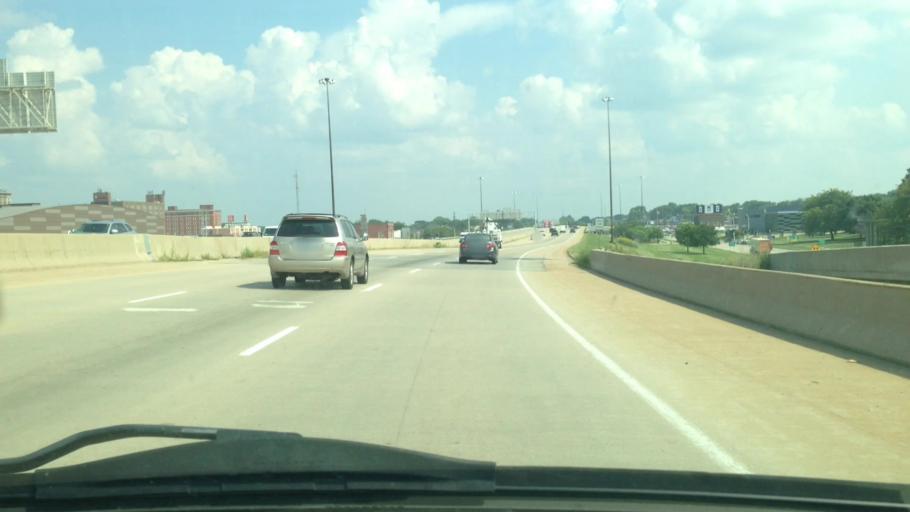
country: US
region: Iowa
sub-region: Black Hawk County
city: Waterloo
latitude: 42.4962
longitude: -92.3468
